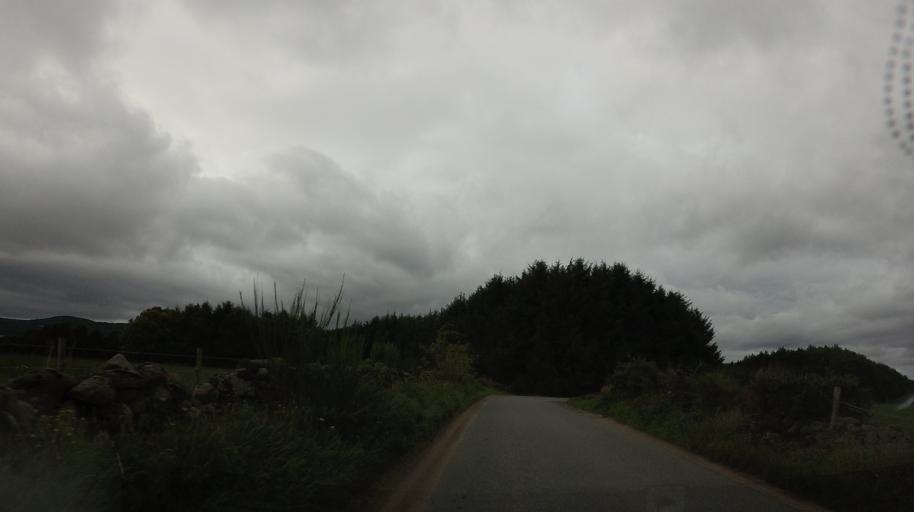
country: GB
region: Scotland
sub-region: Aberdeenshire
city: Banchory
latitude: 57.0768
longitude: -2.4612
